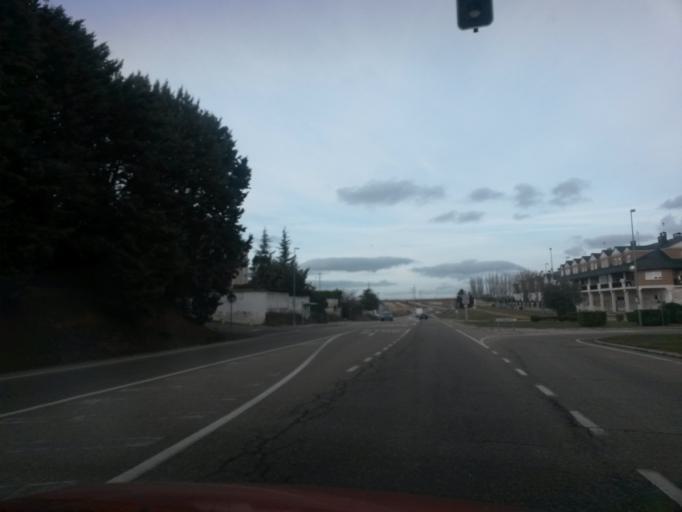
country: ES
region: Castille and Leon
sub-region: Provincia de Salamanca
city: Villares de la Reina
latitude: 40.9931
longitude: -5.6580
